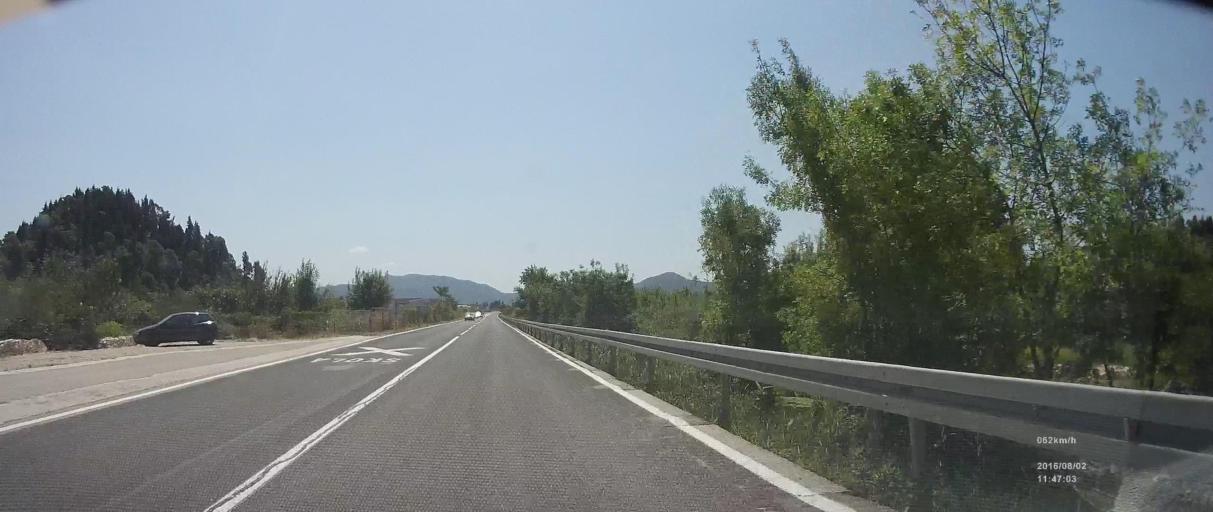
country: HR
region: Dubrovacko-Neretvanska
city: Komin
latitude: 43.0478
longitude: 17.4794
